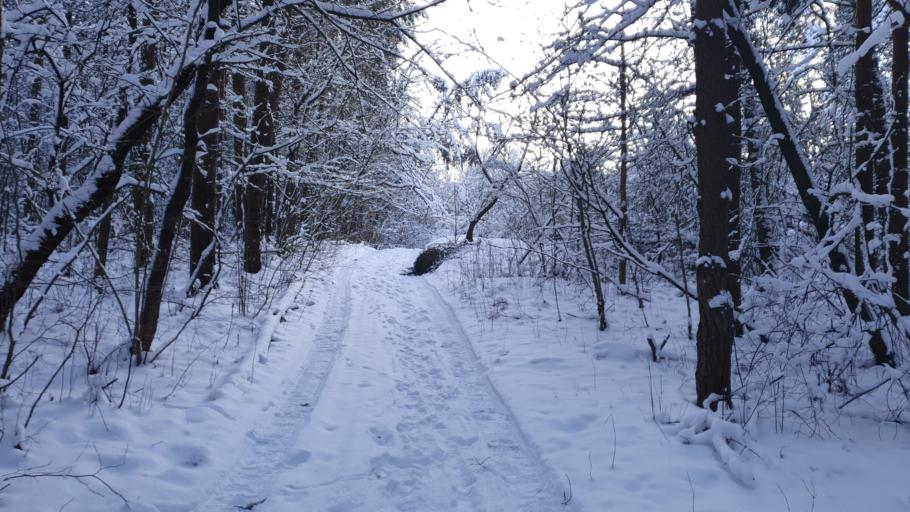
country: LT
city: Skaidiskes
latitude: 54.6427
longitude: 25.4168
